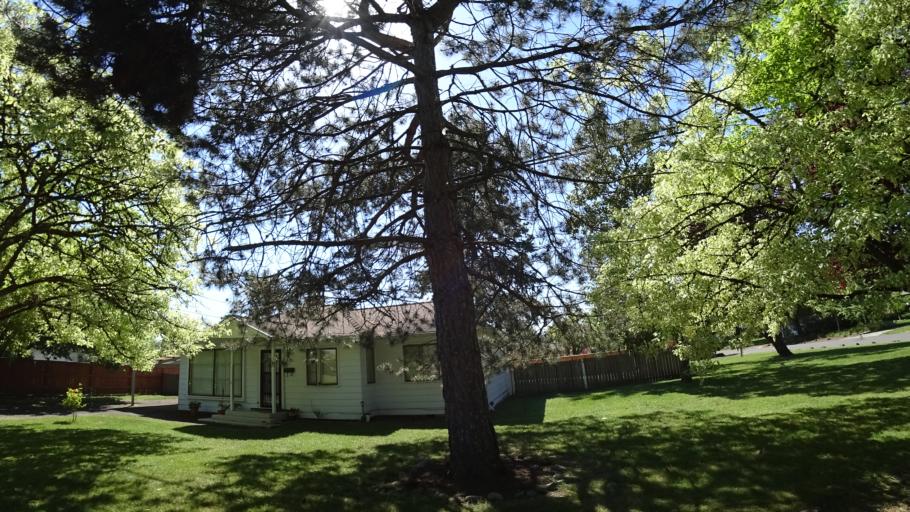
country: US
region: Oregon
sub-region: Washington County
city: Cedar Hills
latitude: 45.4970
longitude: -122.8015
